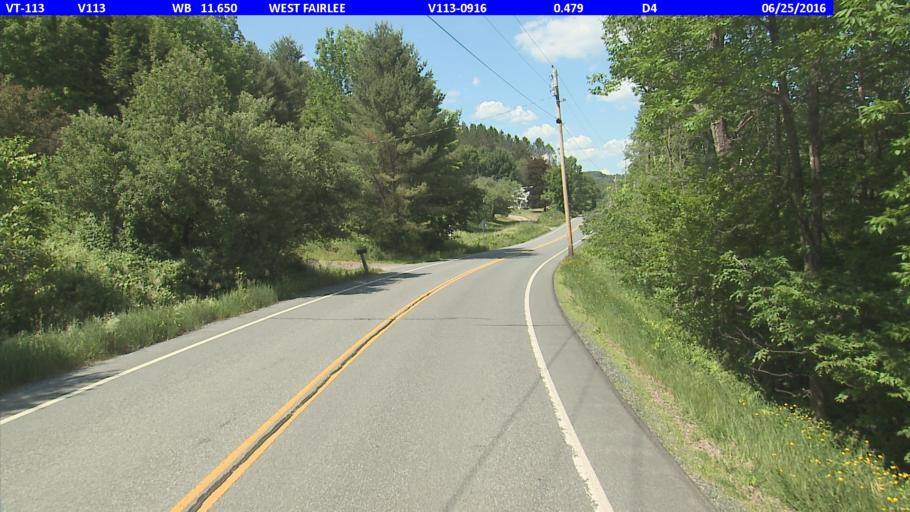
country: US
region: New Hampshire
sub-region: Grafton County
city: Orford
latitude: 43.9297
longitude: -72.2687
